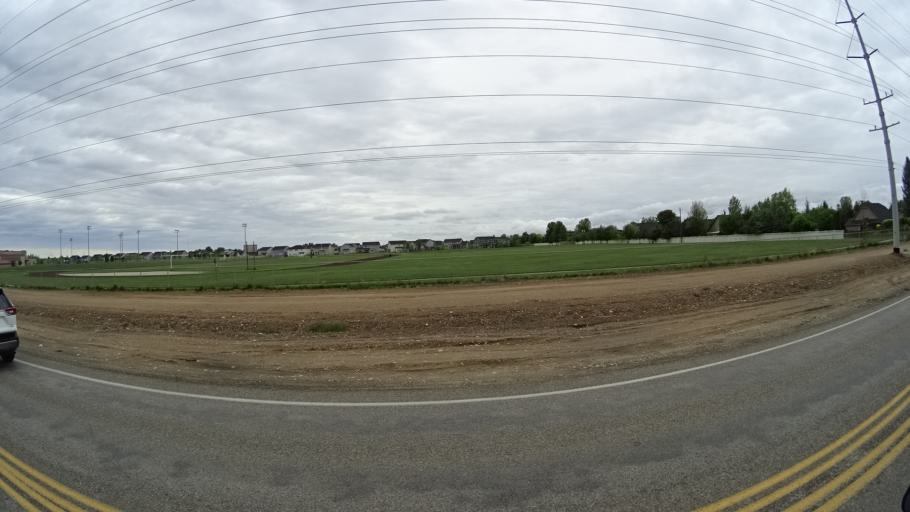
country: US
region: Idaho
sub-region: Ada County
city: Meridian
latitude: 43.6482
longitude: -116.3872
